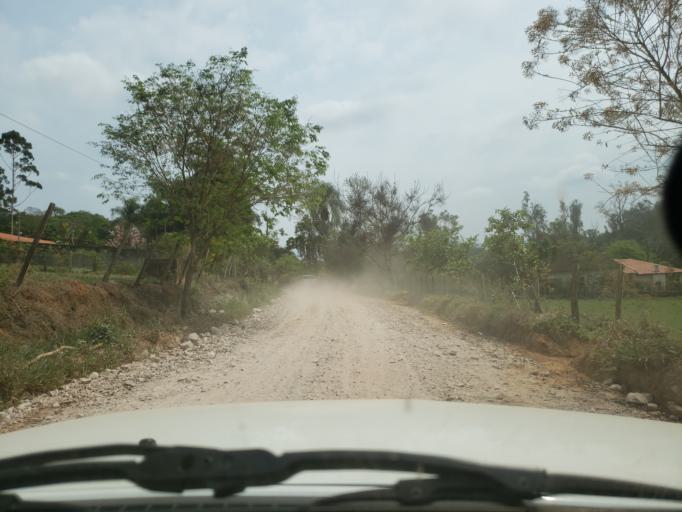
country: BR
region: Minas Gerais
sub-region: Jacutinga
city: Jacutinga
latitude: -22.3071
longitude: -46.6072
